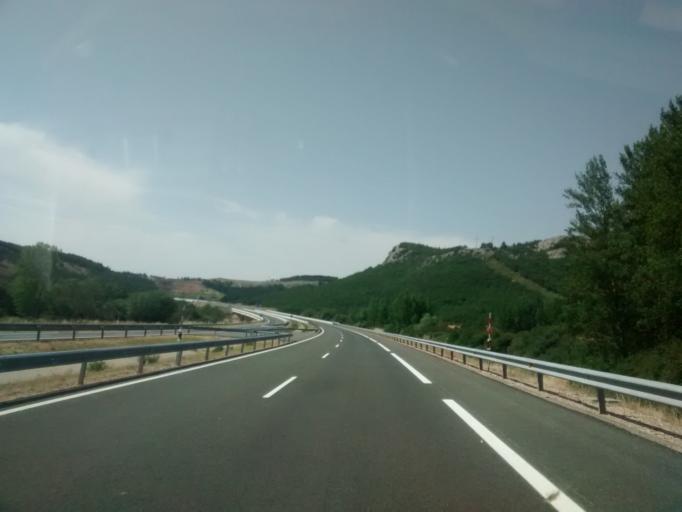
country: ES
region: Castille and Leon
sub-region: Provincia de Palencia
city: Alar del Rey
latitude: 42.6985
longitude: -4.2961
